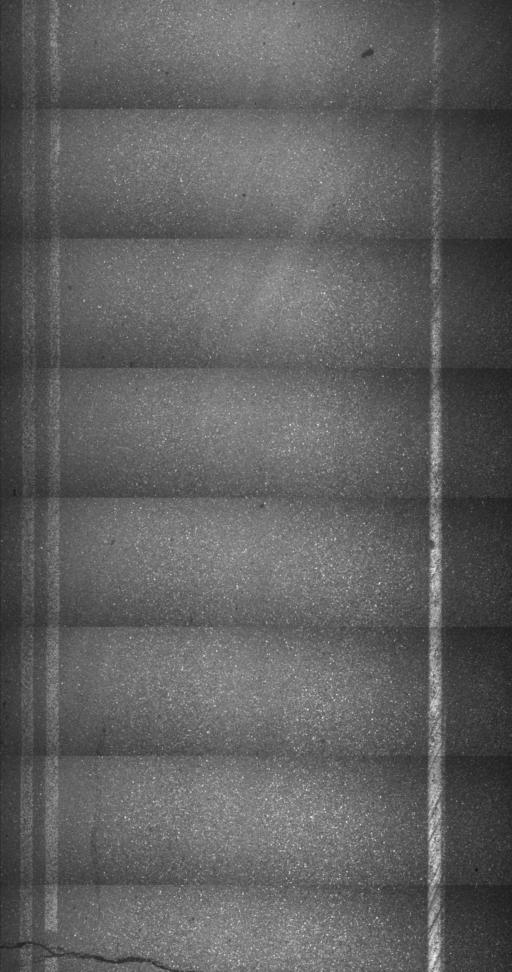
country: US
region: New Hampshire
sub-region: Cheshire County
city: Hinsdale
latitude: 42.7788
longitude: -72.5223
